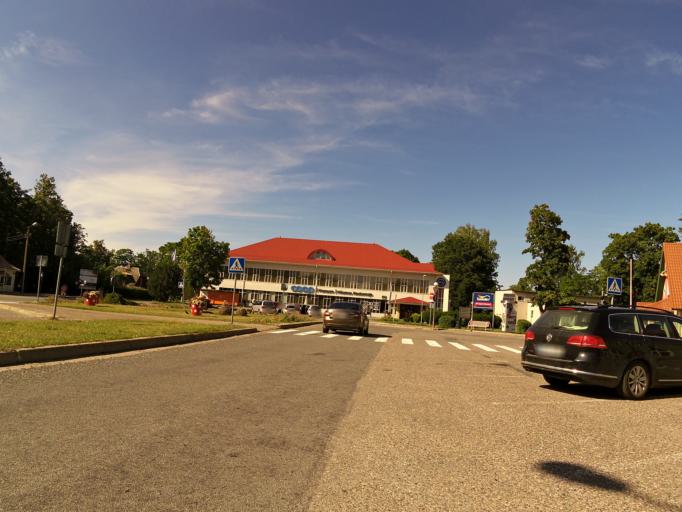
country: EE
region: Hiiumaa
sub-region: Kaerdla linn
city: Kardla
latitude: 58.9978
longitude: 22.7471
